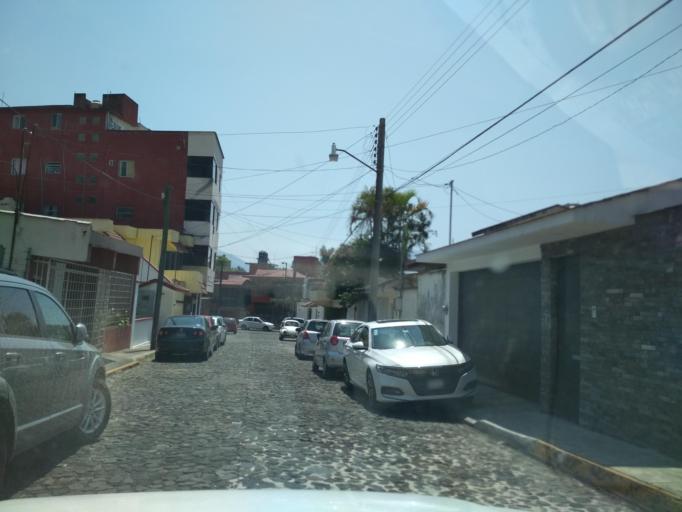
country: MX
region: Veracruz
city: Orizaba
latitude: 18.8518
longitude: -97.0869
